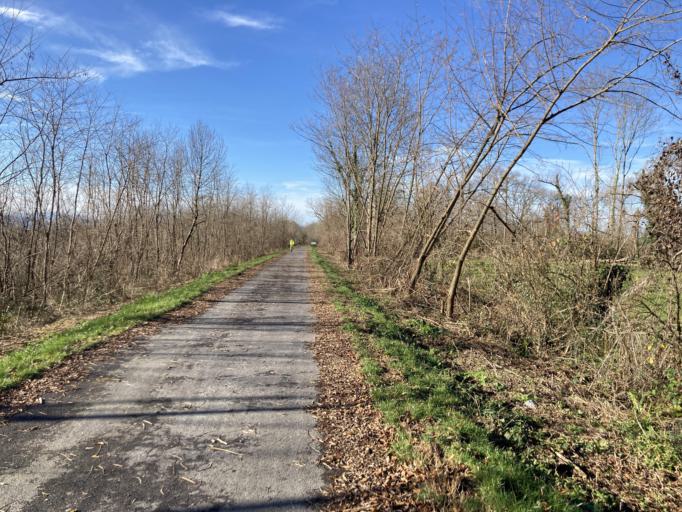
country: FR
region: Aquitaine
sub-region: Departement des Pyrenees-Atlantiques
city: Arudy
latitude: 43.1419
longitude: -0.4523
